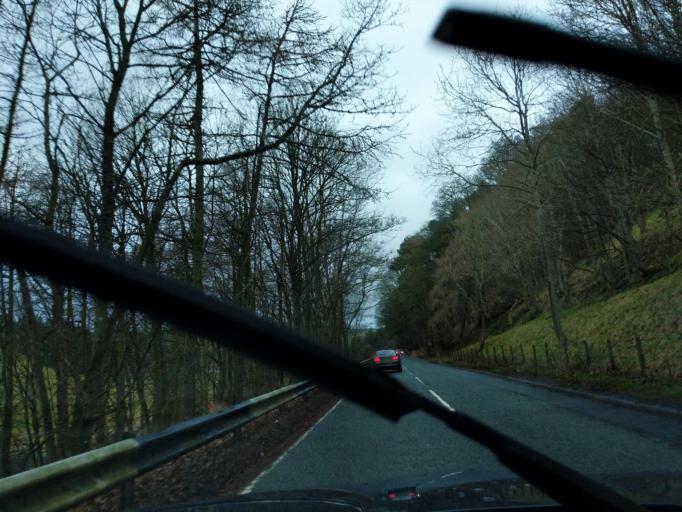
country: GB
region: Scotland
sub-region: The Scottish Borders
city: Galashiels
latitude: 55.6457
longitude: -2.8555
